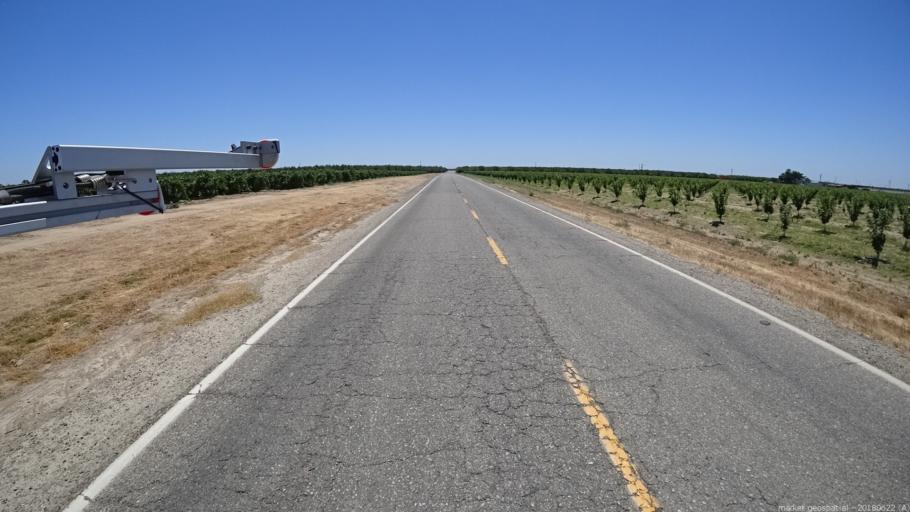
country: US
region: California
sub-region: Madera County
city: Parksdale
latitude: 36.9047
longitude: -119.9924
